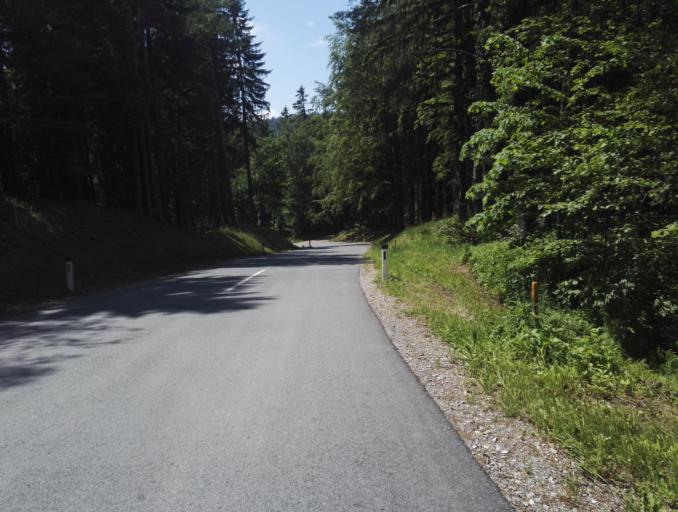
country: AT
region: Styria
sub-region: Politischer Bezirk Graz-Umgebung
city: Sankt Radegund bei Graz
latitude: 47.1840
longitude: 15.4819
